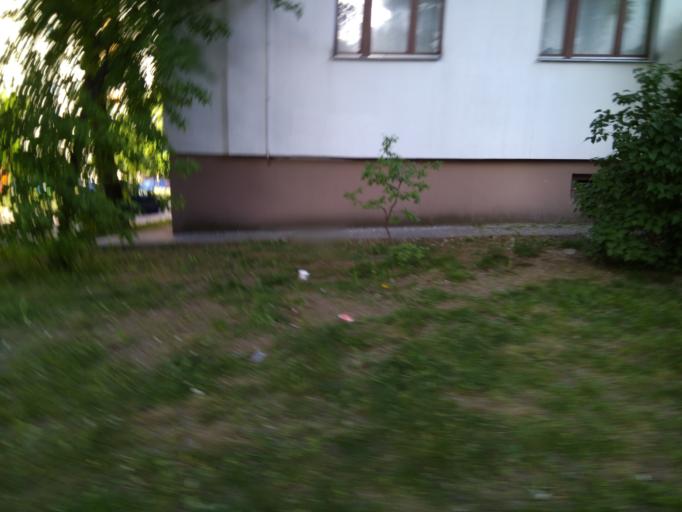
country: BY
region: Minsk
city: Minsk
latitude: 53.9108
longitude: 27.5316
